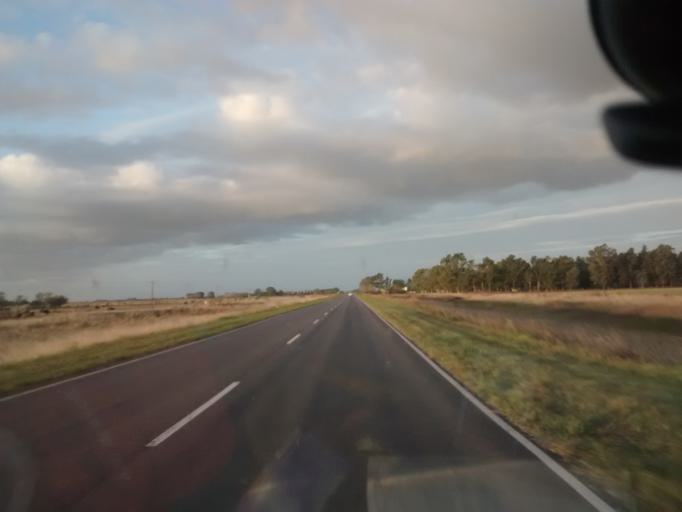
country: AR
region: Buenos Aires
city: Ranchos
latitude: -35.5597
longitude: -58.3974
